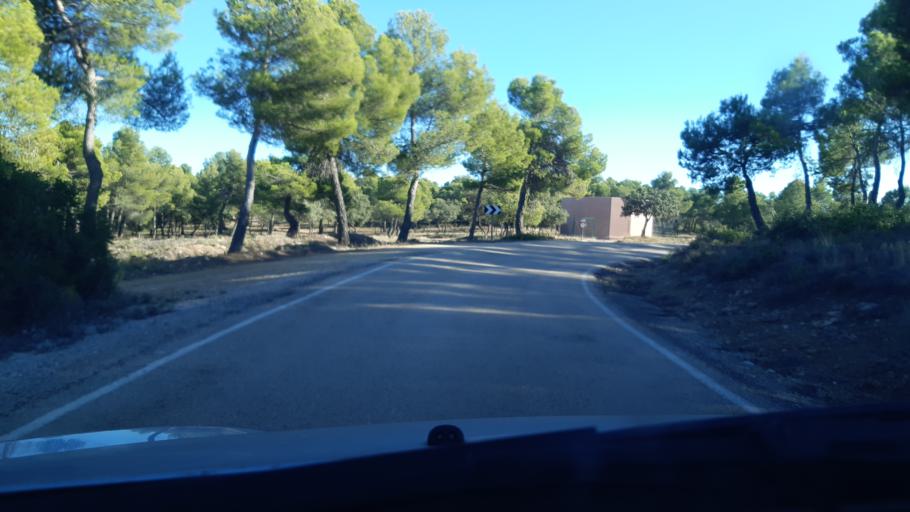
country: ES
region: Aragon
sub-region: Provincia de Teruel
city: Fornoles
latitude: 40.9124
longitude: -0.0180
